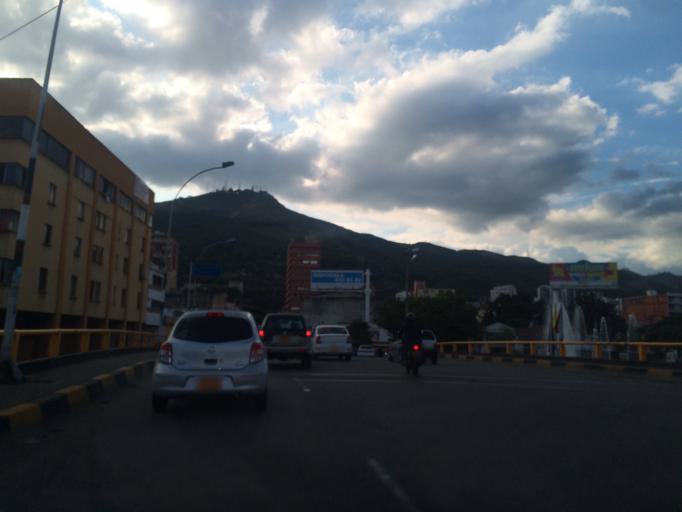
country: CO
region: Valle del Cauca
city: Cali
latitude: 3.4570
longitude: -76.5311
